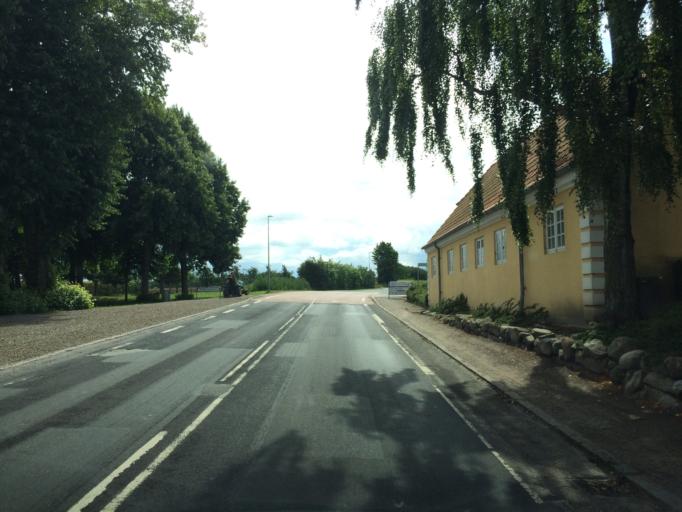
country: DK
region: South Denmark
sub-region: Faaborg-Midtfyn Kommune
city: Faaborg
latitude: 55.1934
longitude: 10.2474
